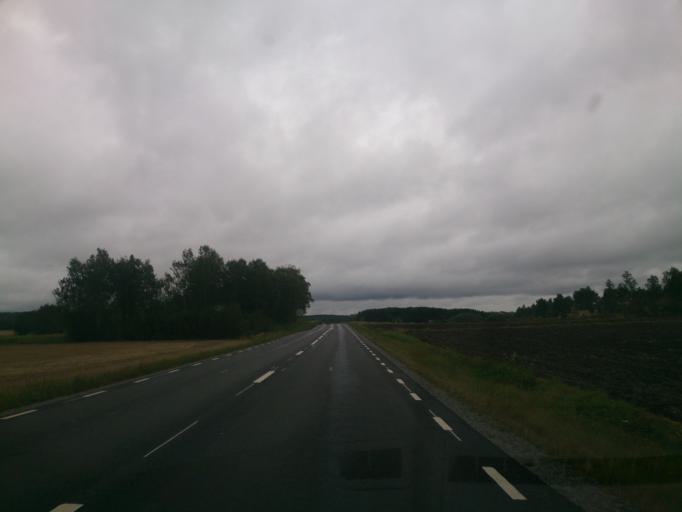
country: SE
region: OEstergoetland
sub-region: Norrkopings Kommun
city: Krokek
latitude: 58.5754
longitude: 16.4599
